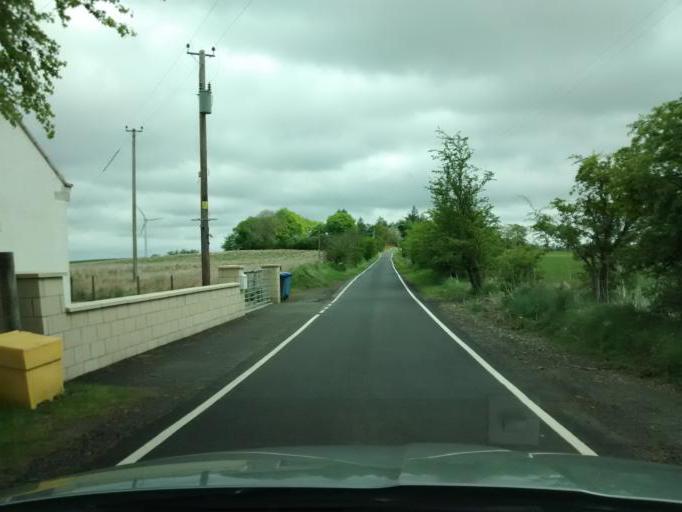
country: GB
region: Scotland
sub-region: North Lanarkshire
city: Harthill
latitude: 55.8819
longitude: -3.7339
